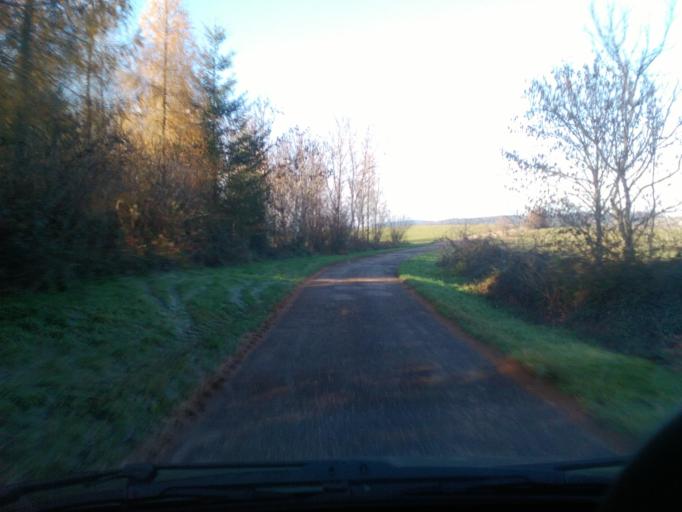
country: FR
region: Lorraine
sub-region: Departement des Vosges
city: Saint-Die-des-Vosges
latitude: 48.3327
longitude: 6.9686
